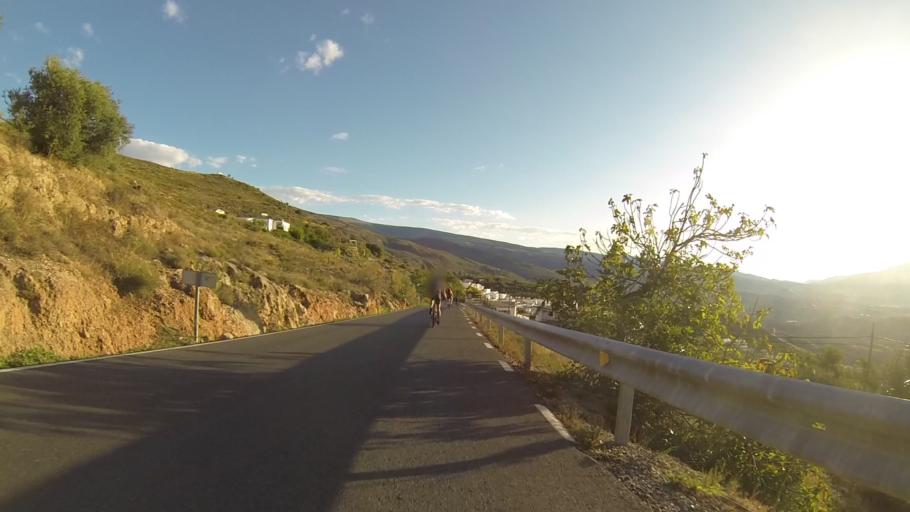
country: ES
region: Andalusia
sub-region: Provincia de Granada
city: Valor
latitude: 36.9800
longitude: -3.1229
